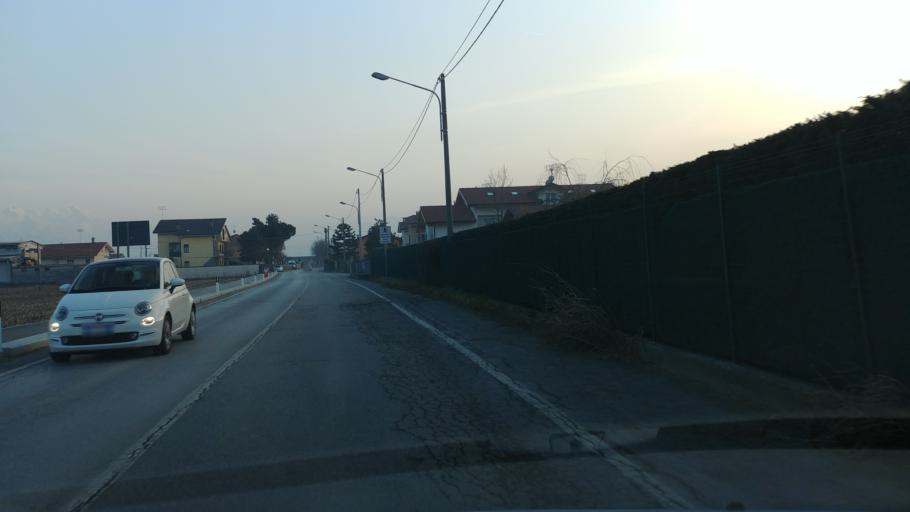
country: IT
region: Piedmont
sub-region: Provincia di Cuneo
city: Roata Rossi
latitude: 44.4302
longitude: 7.5063
